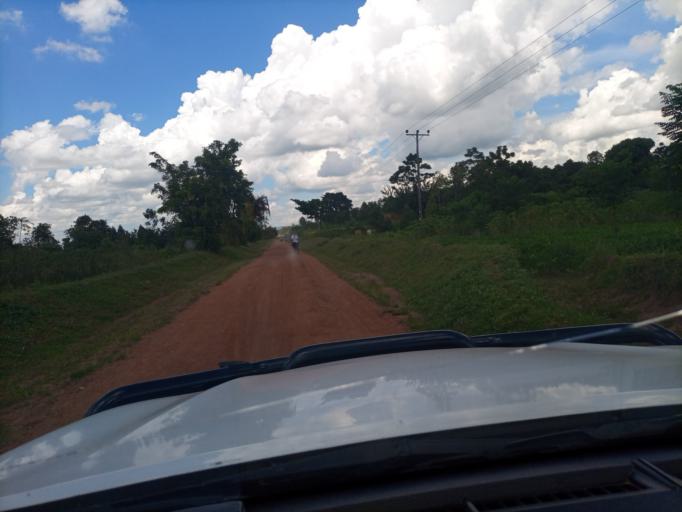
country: UG
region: Eastern Region
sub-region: Tororo District
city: Tororo
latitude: 0.6758
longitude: 34.0057
